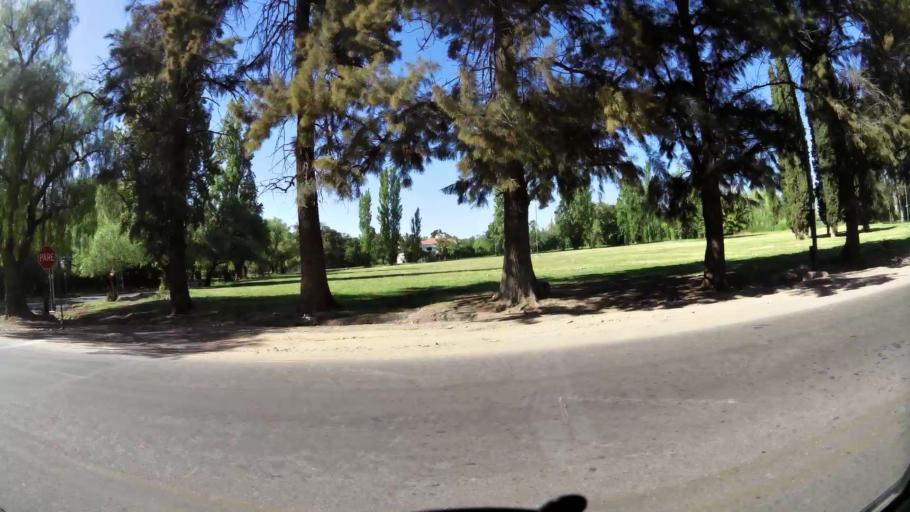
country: AR
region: Mendoza
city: Mendoza
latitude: -32.8928
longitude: -68.8729
